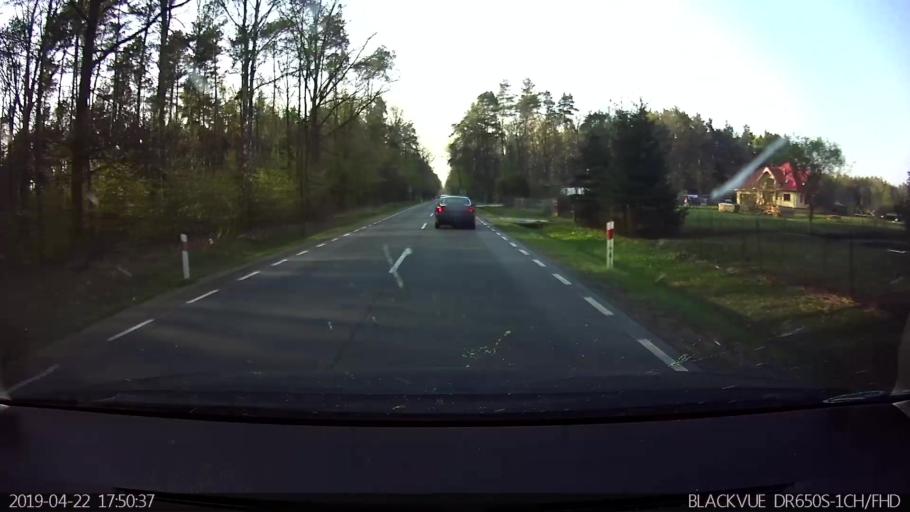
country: PL
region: Masovian Voivodeship
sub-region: Powiat wegrowski
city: Wegrow
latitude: 52.4268
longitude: 22.0004
